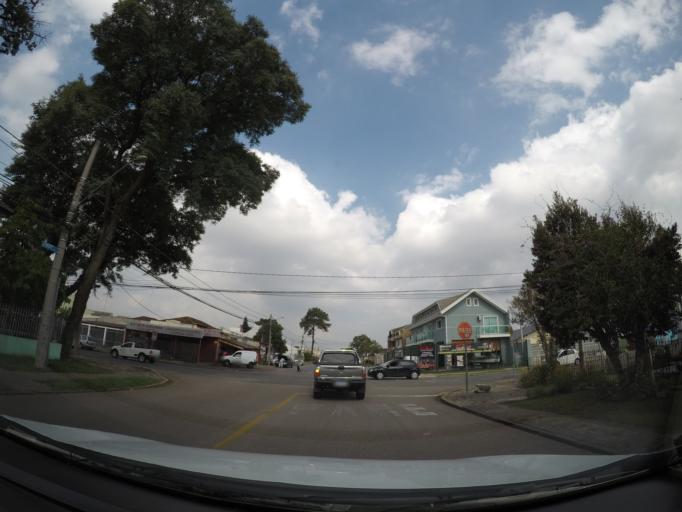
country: BR
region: Parana
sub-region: Curitiba
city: Curitiba
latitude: -25.4781
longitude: -49.2544
